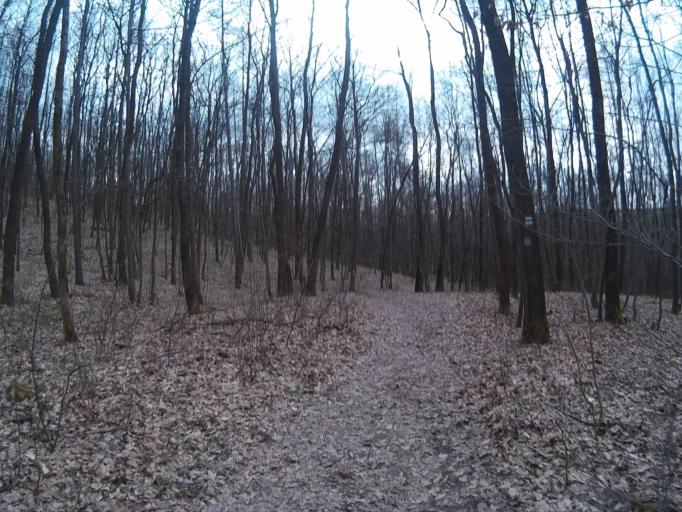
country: HU
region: Pest
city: Vac
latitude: 47.8482
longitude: 19.1127
